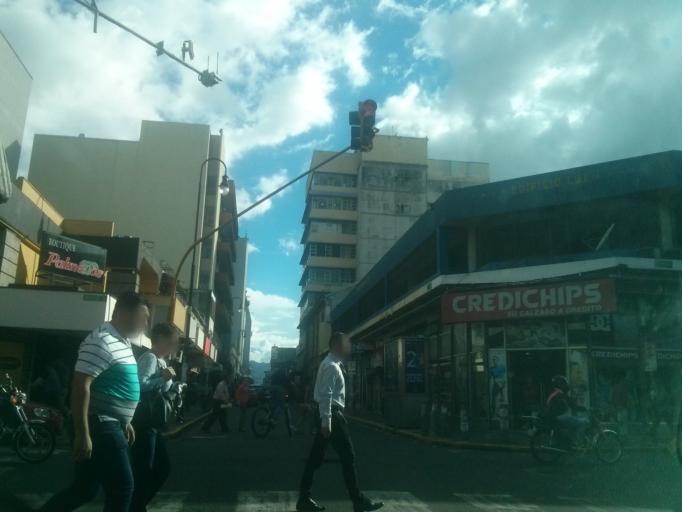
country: CR
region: San Jose
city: San Jose
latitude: 9.9349
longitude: -84.0781
